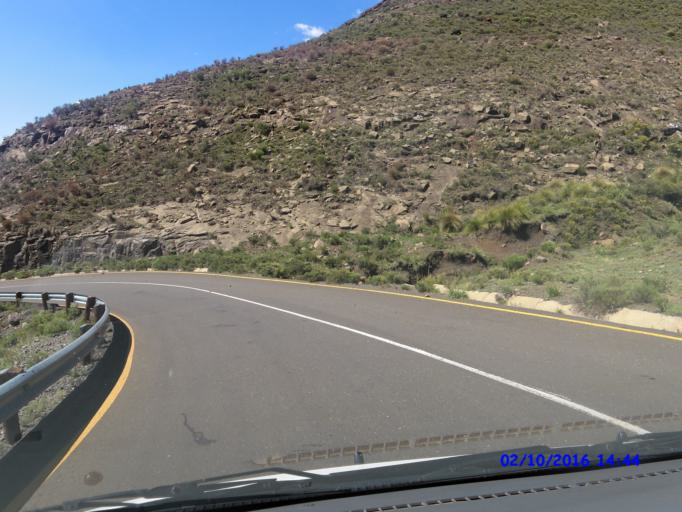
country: LS
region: Maseru
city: Nako
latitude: -29.5229
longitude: 28.0617
